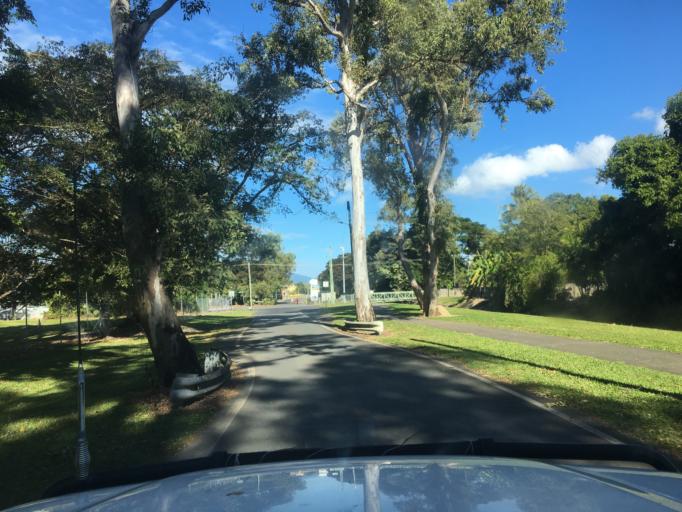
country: AU
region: Queensland
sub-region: Cairns
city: Woree
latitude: -16.9255
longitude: 145.7385
